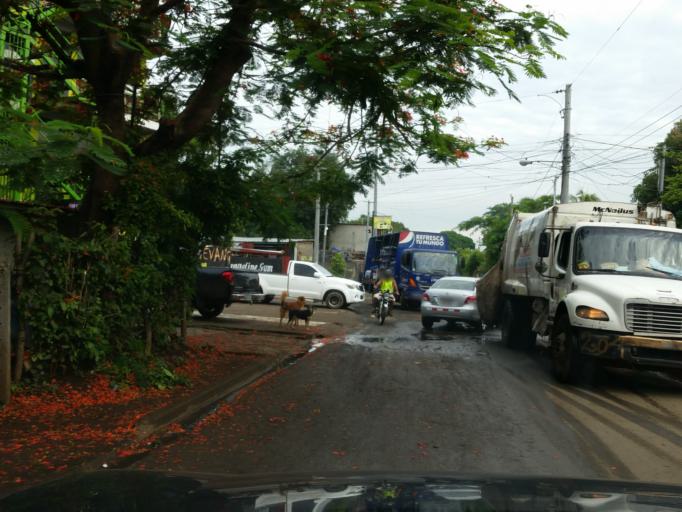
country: NI
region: Managua
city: Managua
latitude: 12.1042
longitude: -86.2199
